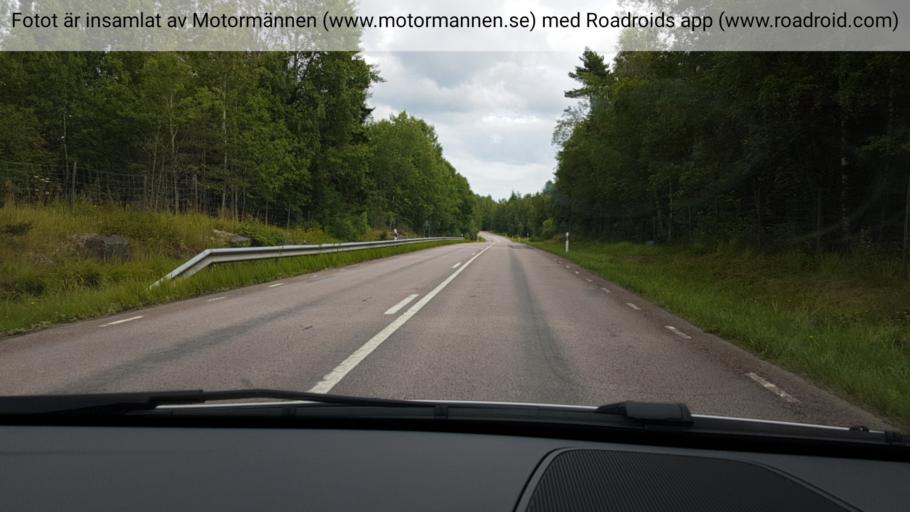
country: SE
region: Uppsala
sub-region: Osthammars Kommun
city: OEsthammar
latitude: 60.2328
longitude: 18.2851
